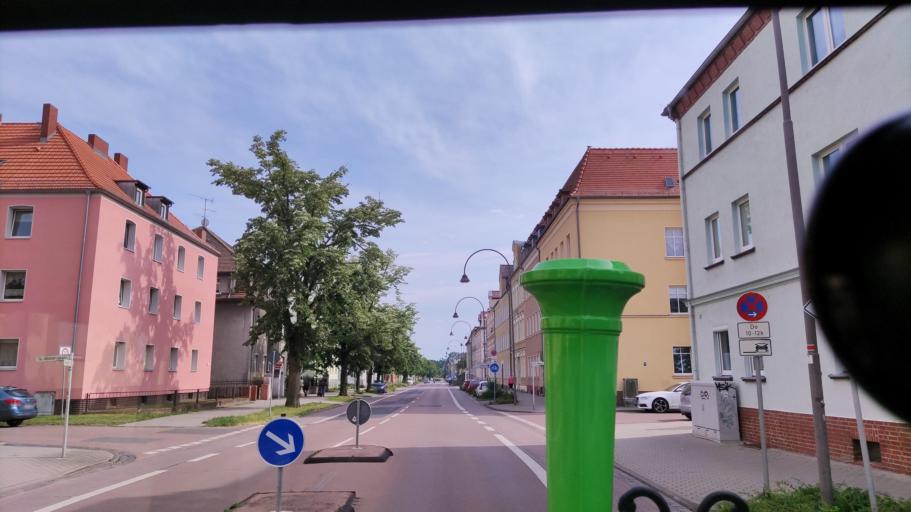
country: DE
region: Saxony-Anhalt
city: Wittenburg
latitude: 51.8733
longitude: 12.6533
